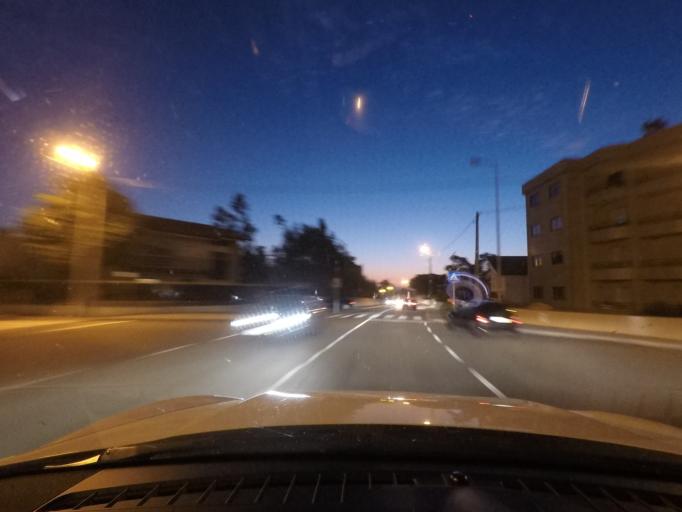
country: PT
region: Porto
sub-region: Vila Nova de Gaia
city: Sao Felix da Marinha
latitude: 41.0404
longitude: -8.6363
